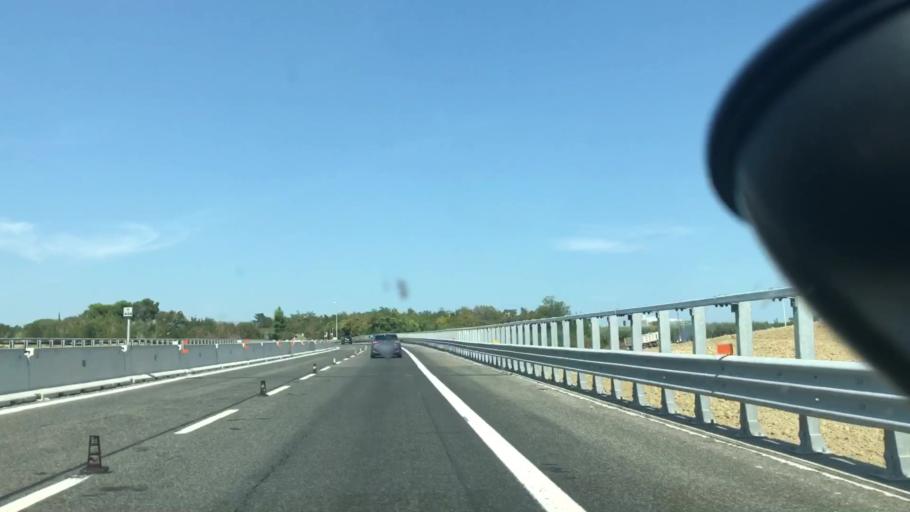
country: IT
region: Abruzzo
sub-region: Provincia di Chieti
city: Marina di Vasto
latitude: 42.0707
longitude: 14.7240
